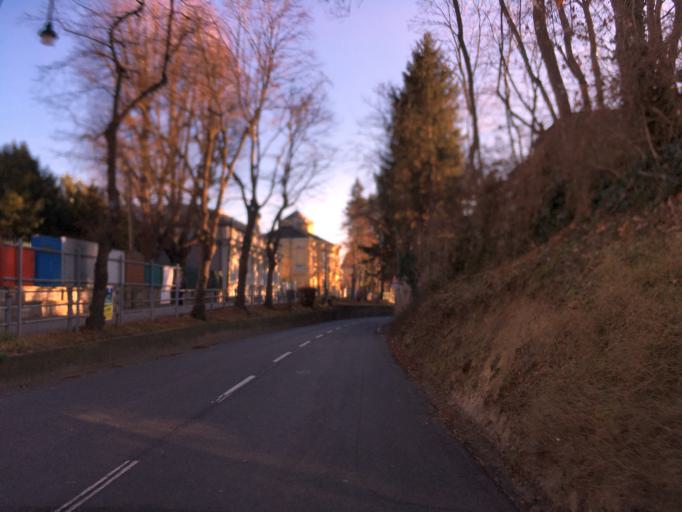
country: AT
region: Lower Austria
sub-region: Politischer Bezirk Wien-Umgebung
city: Klosterneuburg
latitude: 48.3274
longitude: 16.3022
